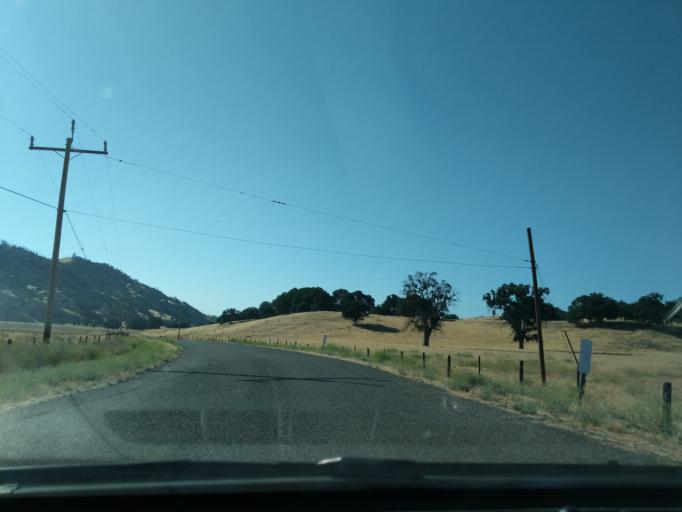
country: US
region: California
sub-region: San Luis Obispo County
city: San Miguel
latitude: 36.1273
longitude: -120.7390
